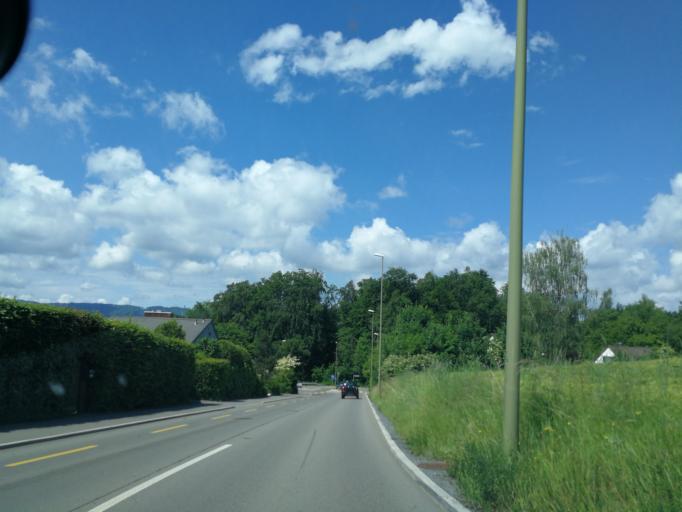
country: CH
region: Zurich
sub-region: Bezirk Meilen
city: Kuesnacht / Itschnach
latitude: 47.3270
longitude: 8.5964
